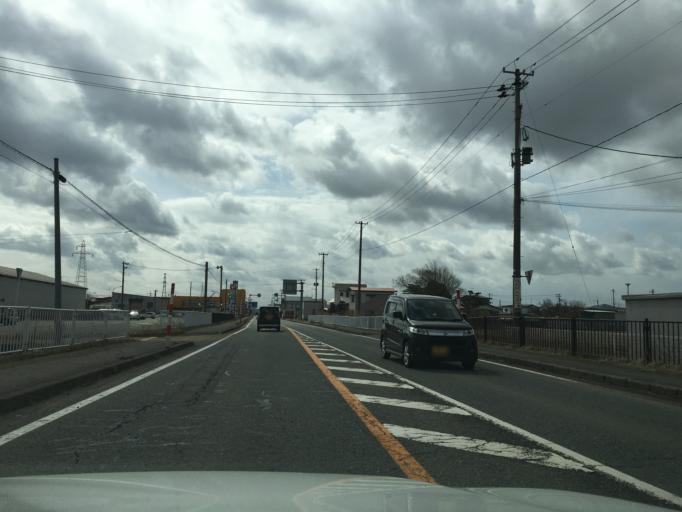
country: JP
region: Akita
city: Tenno
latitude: 39.9481
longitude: 140.0835
